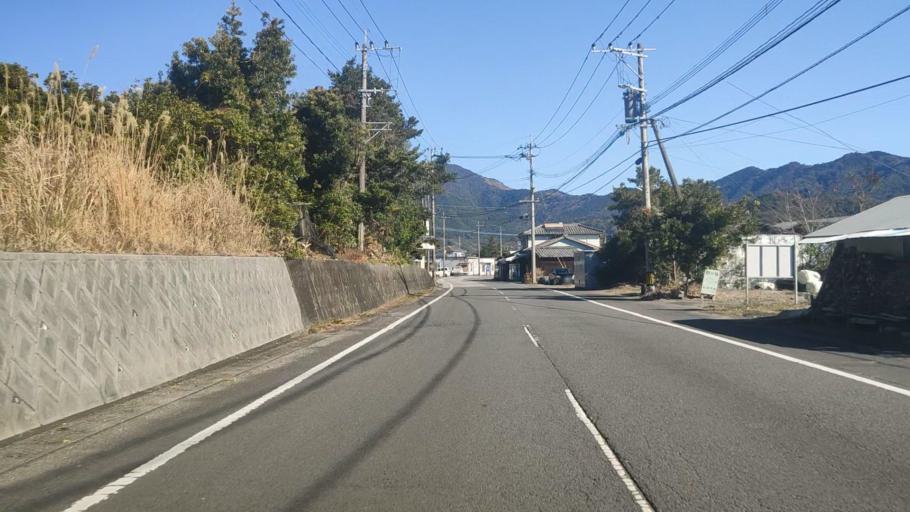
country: JP
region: Oita
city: Saiki
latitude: 32.8037
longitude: 131.8884
